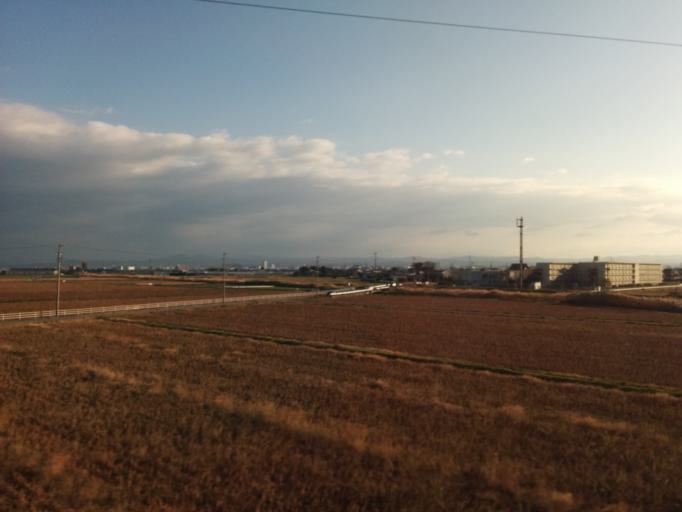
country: JP
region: Aichi
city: Anjo
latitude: 34.9266
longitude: 137.0994
